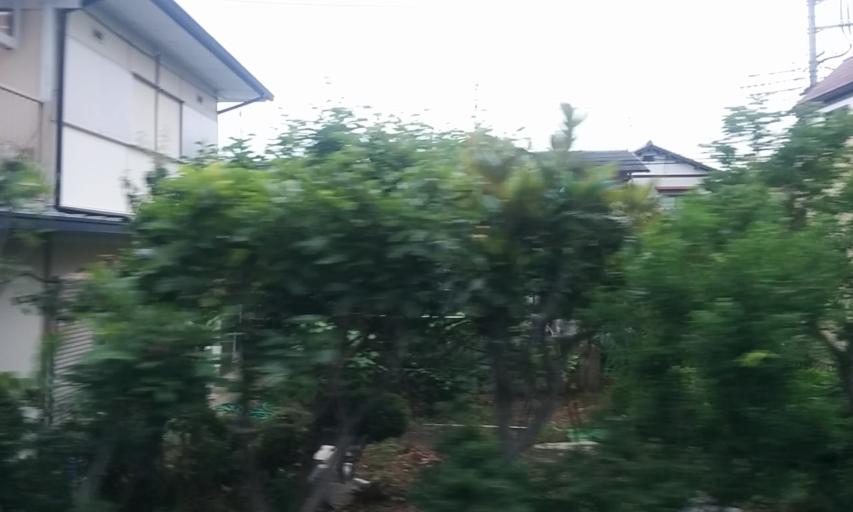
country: JP
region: Chiba
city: Nagareyama
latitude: 35.8386
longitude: 139.9138
